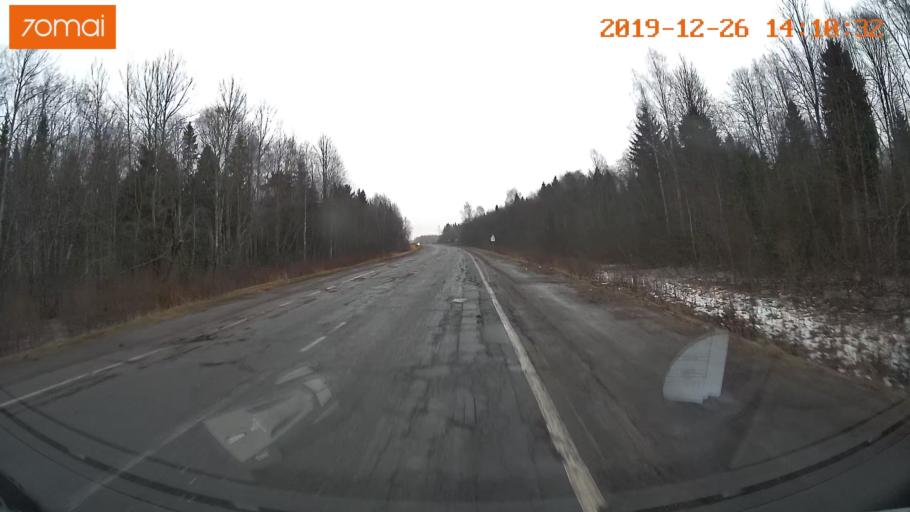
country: RU
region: Jaroslavl
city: Poshekhon'ye
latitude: 58.5084
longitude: 38.9556
